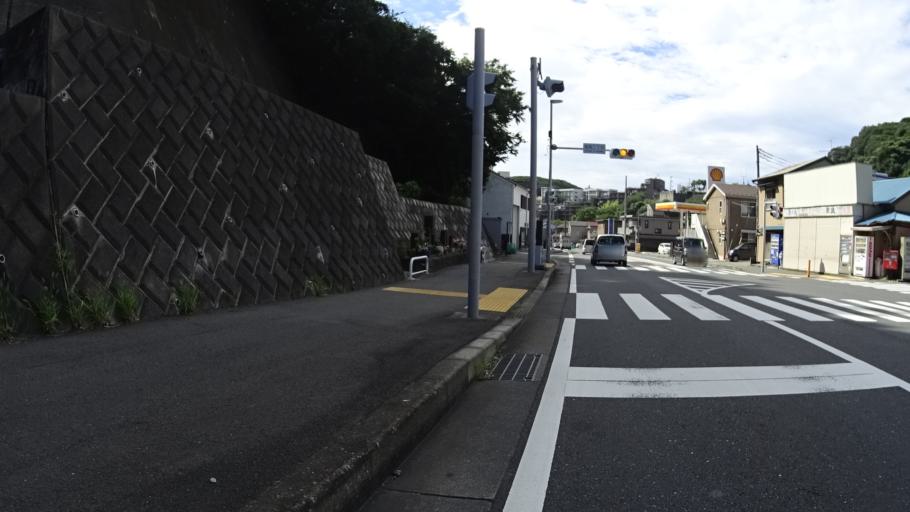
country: JP
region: Kanagawa
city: Yokosuka
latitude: 35.2548
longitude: 139.7096
